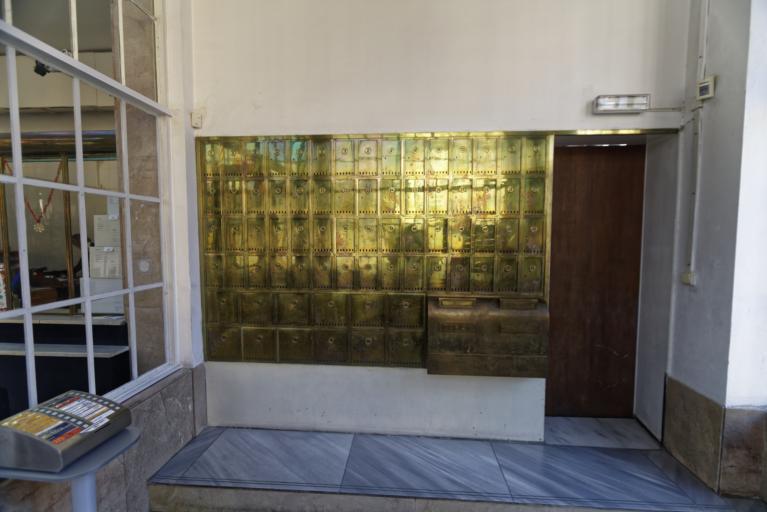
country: CZ
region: Zlin
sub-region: Okres Zlin
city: Luhacovice
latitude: 49.1018
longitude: 17.7597
